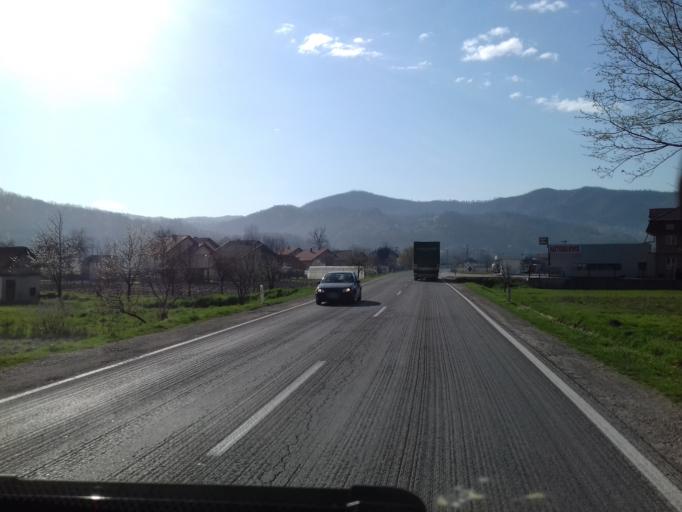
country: BA
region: Federation of Bosnia and Herzegovina
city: Maglaj
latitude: 44.6221
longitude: 18.0962
